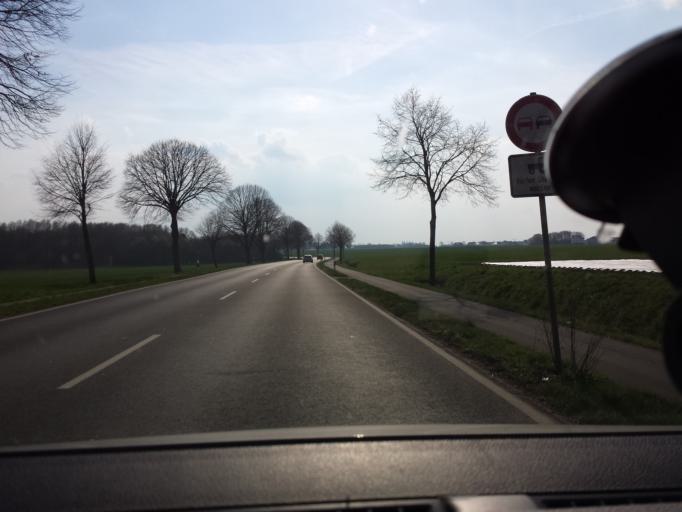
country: DE
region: Lower Saxony
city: Braunschweig
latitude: 52.2674
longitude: 10.4711
